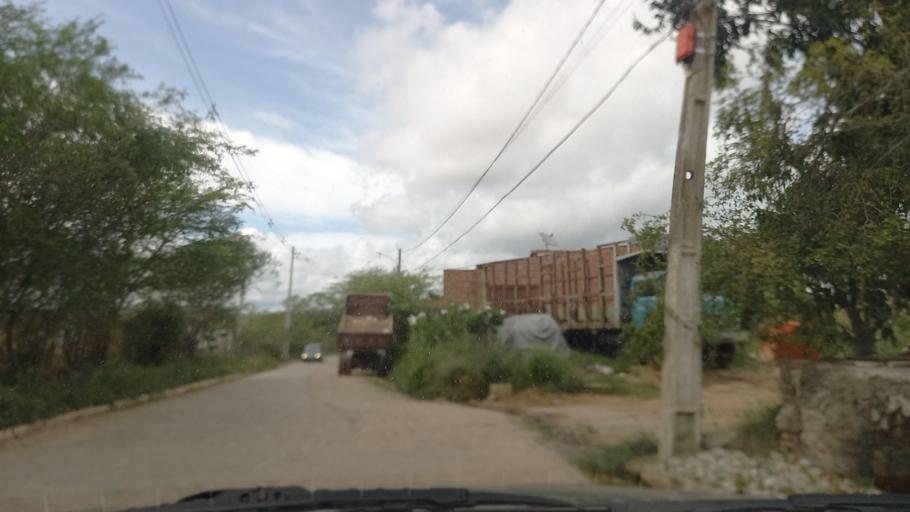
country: BR
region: Pernambuco
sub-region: Gravata
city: Gravata
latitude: -8.1861
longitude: -35.5798
